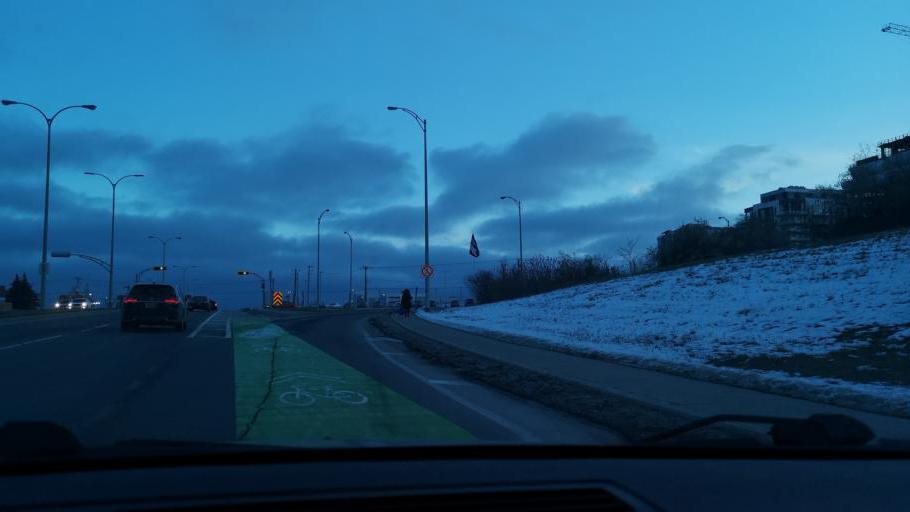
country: CA
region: Quebec
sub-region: Laval
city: Laval
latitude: 45.5673
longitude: -73.7639
